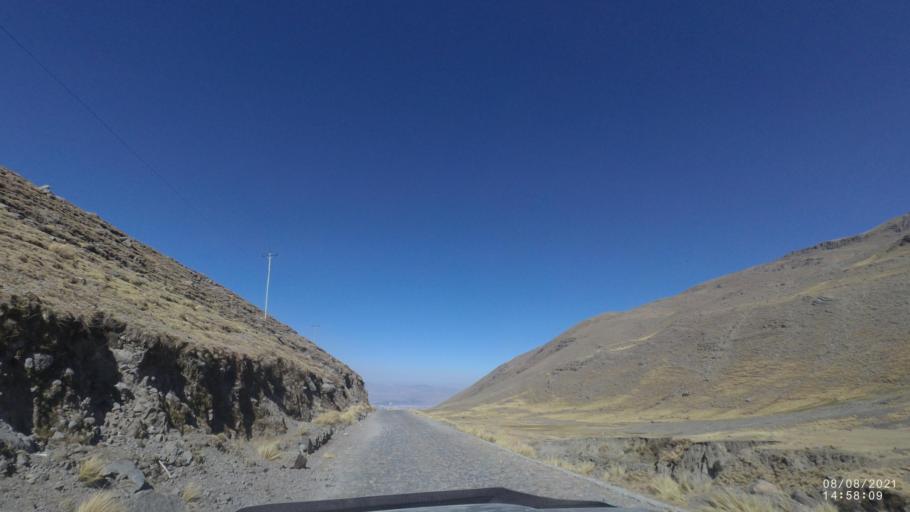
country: BO
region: Cochabamba
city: Sipe Sipe
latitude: -17.2620
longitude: -66.3537
